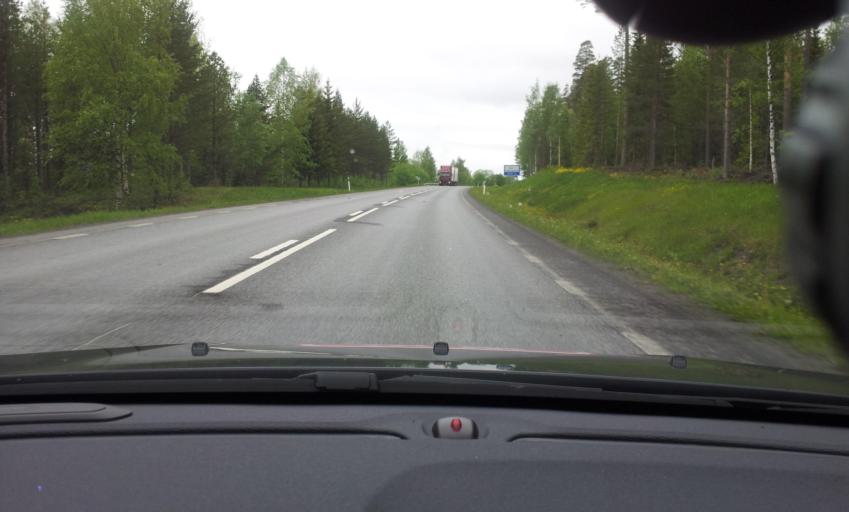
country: SE
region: Jaemtland
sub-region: Krokoms Kommun
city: Krokom
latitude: 63.3142
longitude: 14.1029
